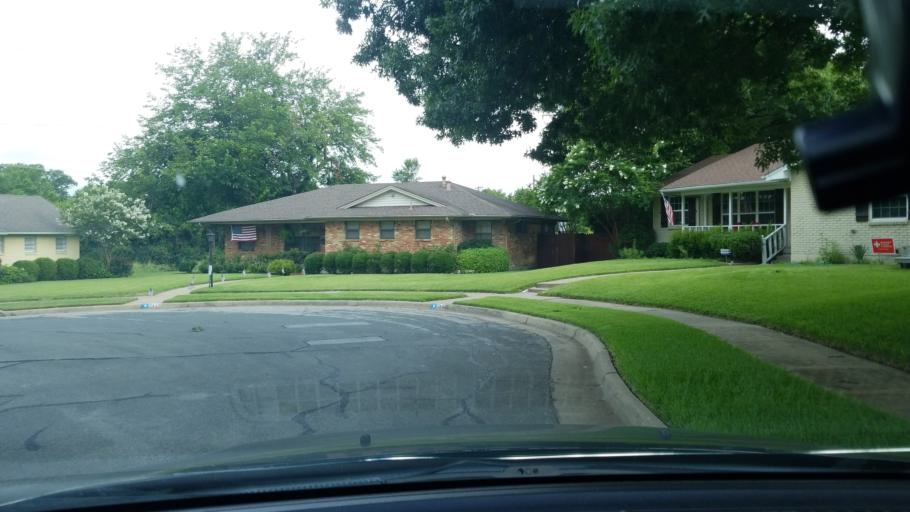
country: US
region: Texas
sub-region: Dallas County
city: Highland Park
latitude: 32.8227
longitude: -96.6954
